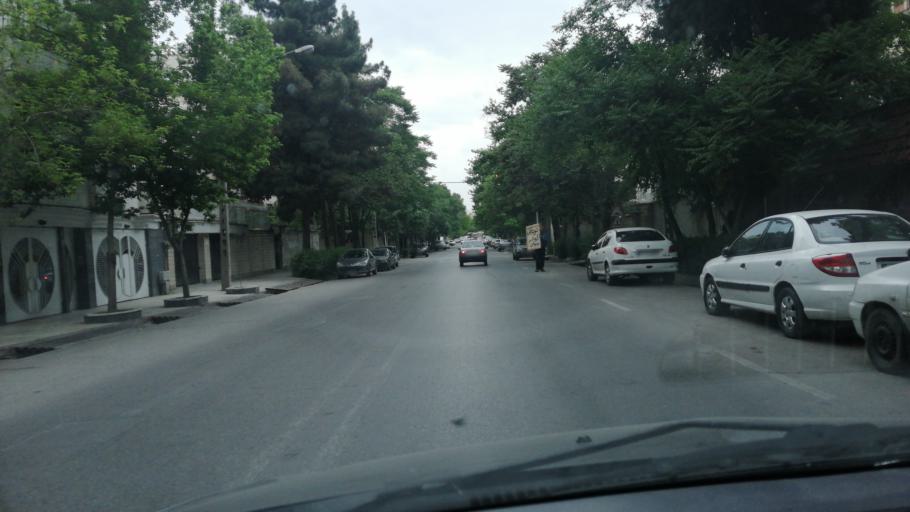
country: IR
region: Razavi Khorasan
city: Mashhad
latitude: 36.2842
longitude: 59.5715
